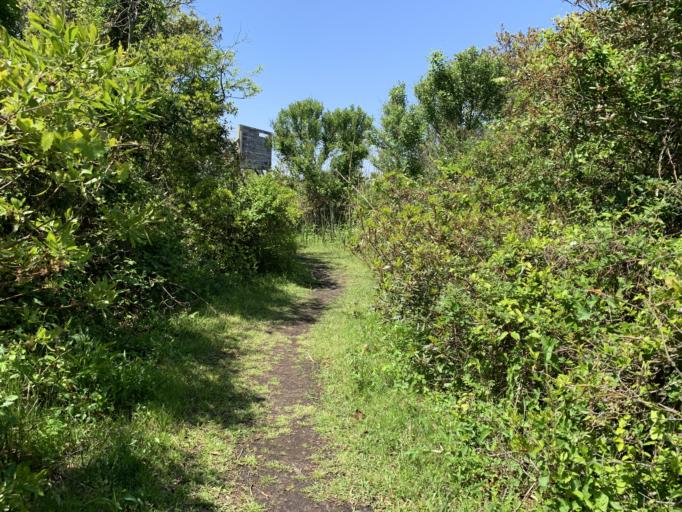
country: US
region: North Carolina
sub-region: Dare County
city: Southern Shores
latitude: 36.2307
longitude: -75.7755
